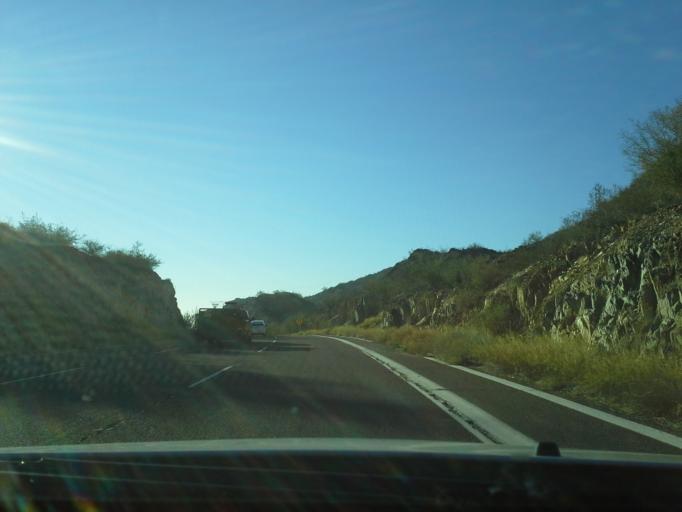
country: US
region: Arizona
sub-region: Maricopa County
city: Glendale
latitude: 33.5919
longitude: -112.0664
